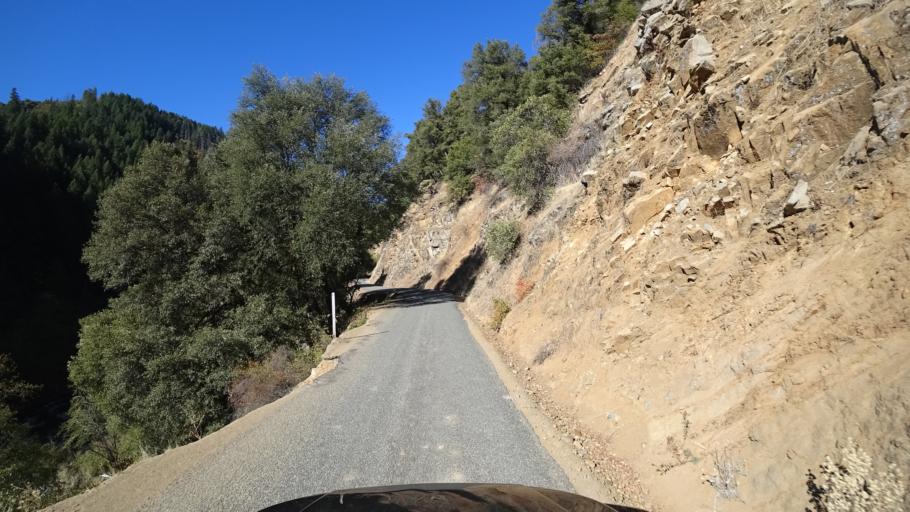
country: US
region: California
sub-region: Humboldt County
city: Willow Creek
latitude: 41.2314
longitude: -123.2551
